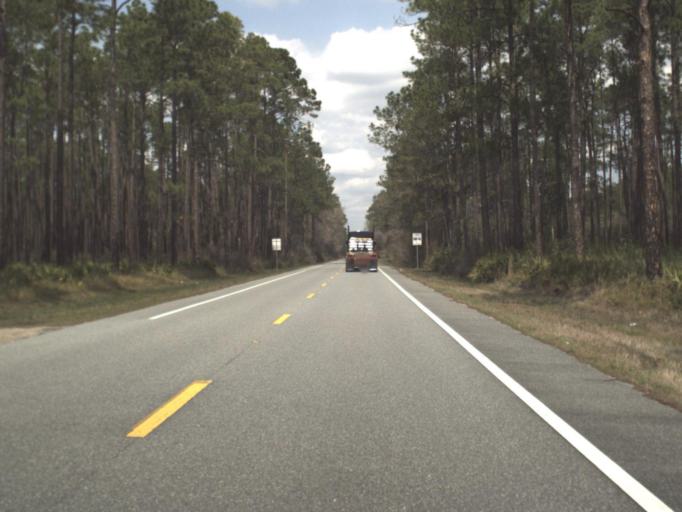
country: US
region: Florida
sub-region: Franklin County
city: Apalachicola
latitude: 29.9056
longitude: -84.9777
